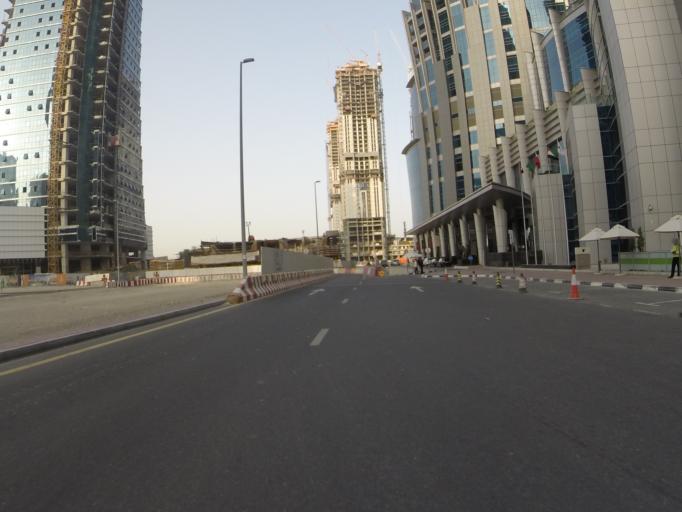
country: AE
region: Dubai
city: Dubai
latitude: 25.1859
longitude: 55.2588
